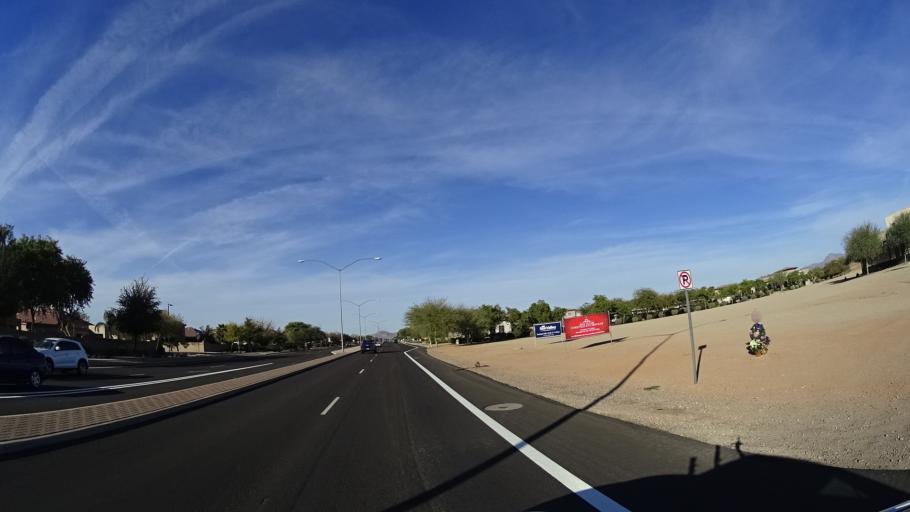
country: US
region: Arizona
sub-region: Pinal County
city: Apache Junction
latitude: 33.3584
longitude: -111.6358
